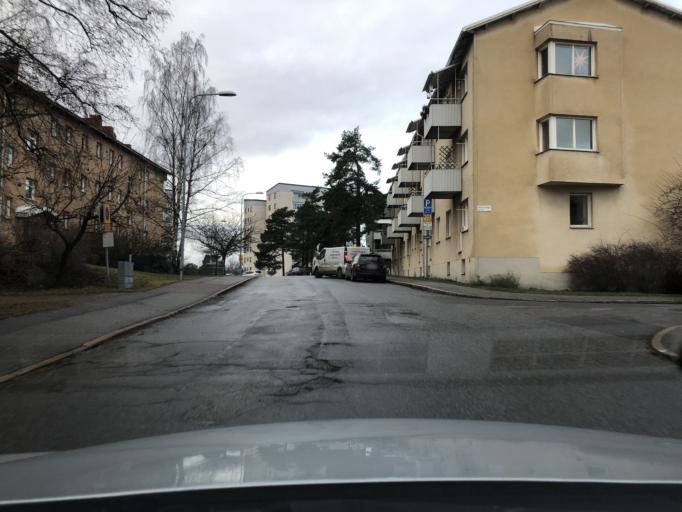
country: SE
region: Stockholm
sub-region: Stockholms Kommun
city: Arsta
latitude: 59.3009
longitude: 18.0548
